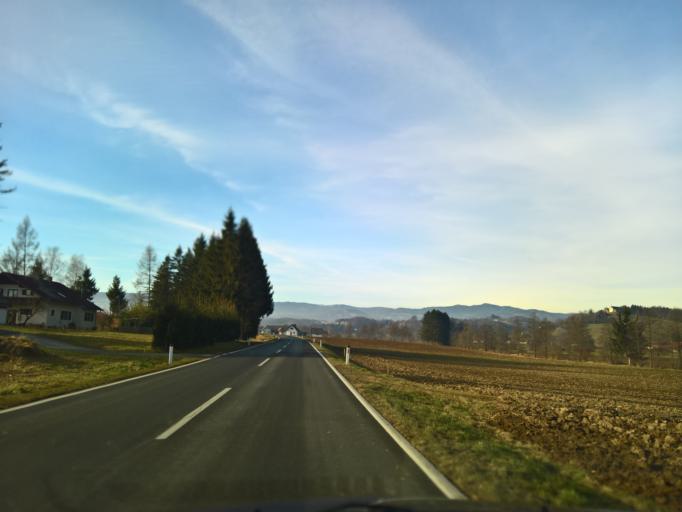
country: AT
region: Styria
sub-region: Politischer Bezirk Deutschlandsberg
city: Pitschgau
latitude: 46.6989
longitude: 15.2988
